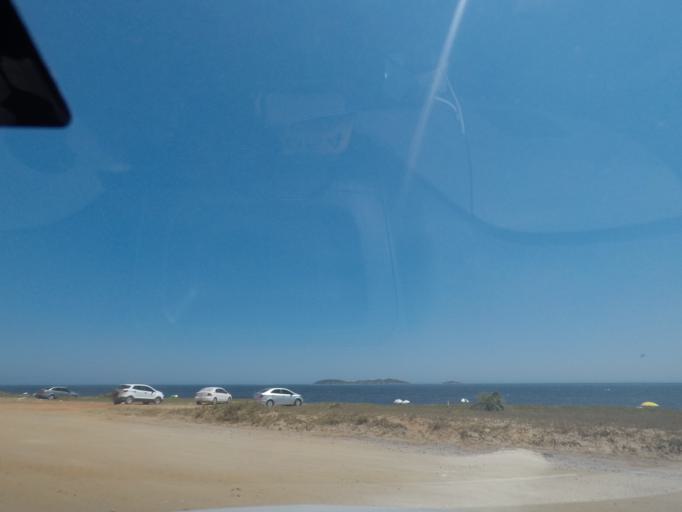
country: BR
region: Rio de Janeiro
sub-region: Marica
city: Marica
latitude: -22.9734
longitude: -42.9307
